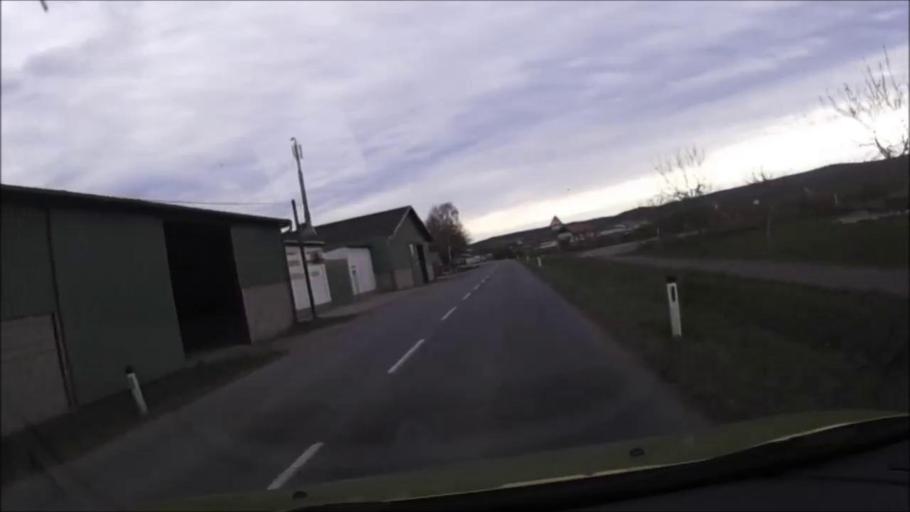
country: AT
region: Burgenland
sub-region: Eisenstadt-Umgebung
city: Leithaprodersdorf
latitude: 47.9361
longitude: 16.4862
